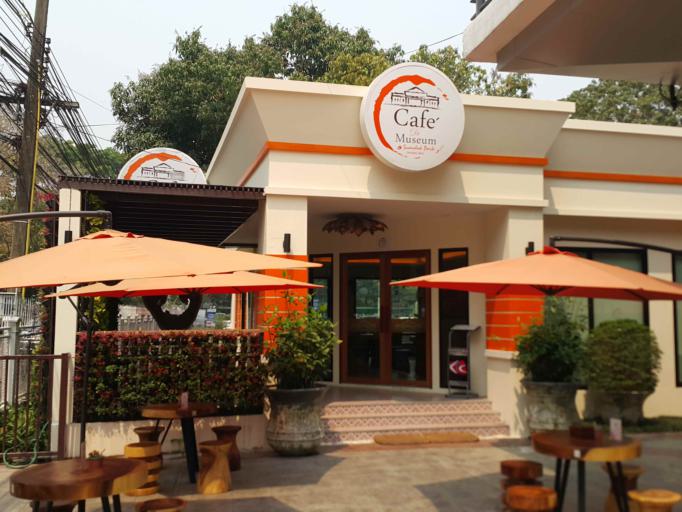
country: TH
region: Chiang Mai
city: Chiang Mai
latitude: 18.7902
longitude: 98.9706
